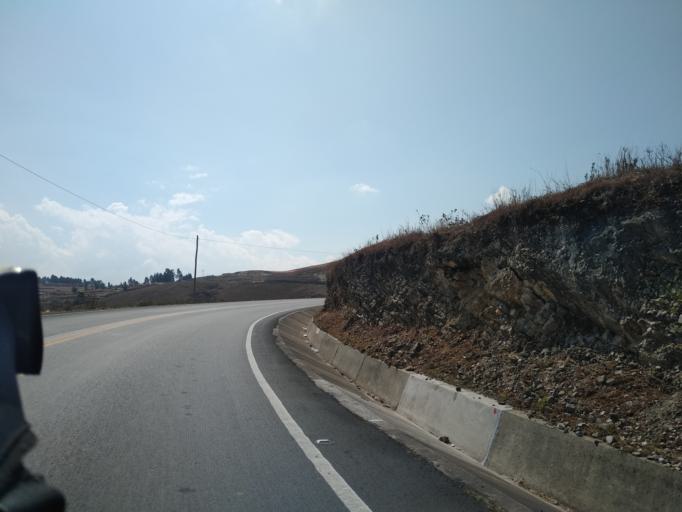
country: PE
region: Cajamarca
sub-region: Provincia de Cajamarca
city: Llacanora
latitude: -7.2062
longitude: -78.3883
